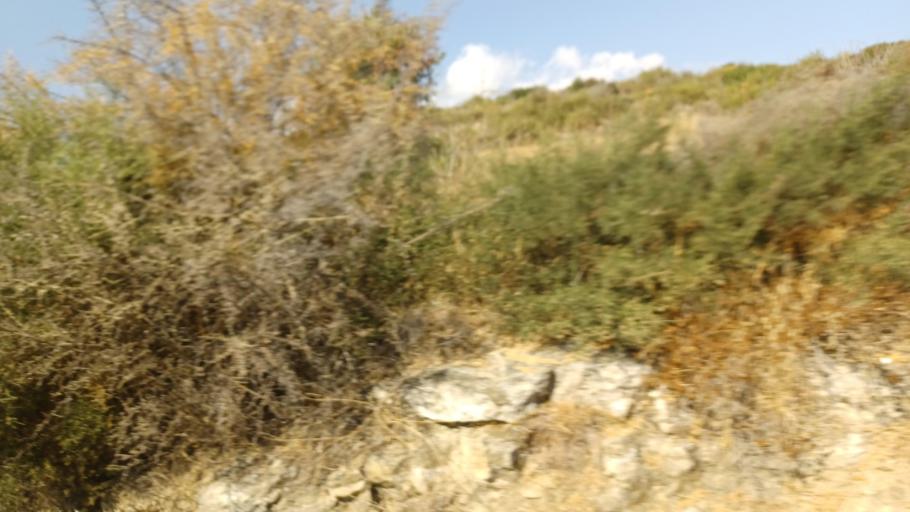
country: CY
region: Pafos
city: Polis
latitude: 34.9845
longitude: 32.4325
